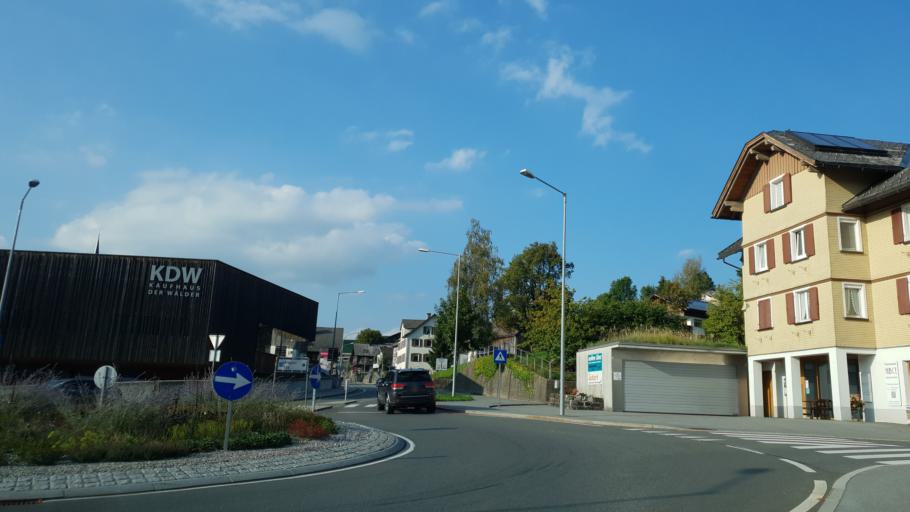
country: AT
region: Vorarlberg
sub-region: Politischer Bezirk Bregenz
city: Egg
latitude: 47.4284
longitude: 9.8974
